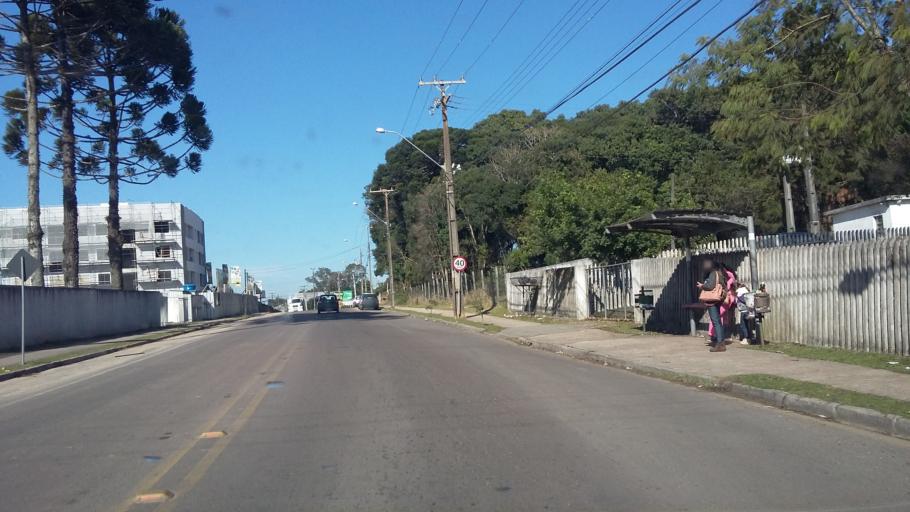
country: BR
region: Parana
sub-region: Campo Largo
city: Campo Largo
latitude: -25.4544
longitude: -49.5415
